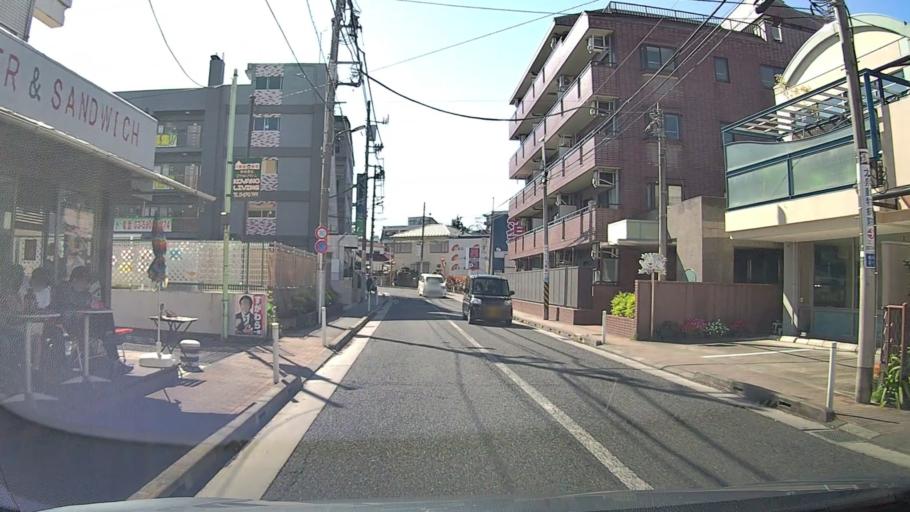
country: JP
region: Saitama
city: Wako
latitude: 35.7517
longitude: 139.5938
